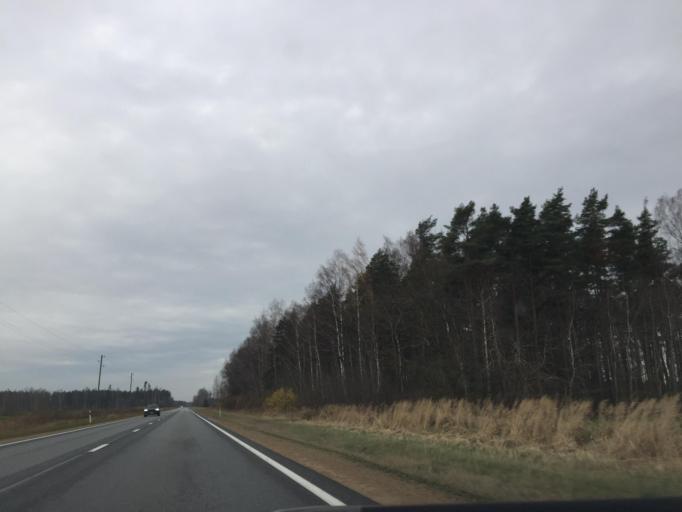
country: LV
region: Jurmala
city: Jurmala
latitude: 56.9059
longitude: 23.7648
